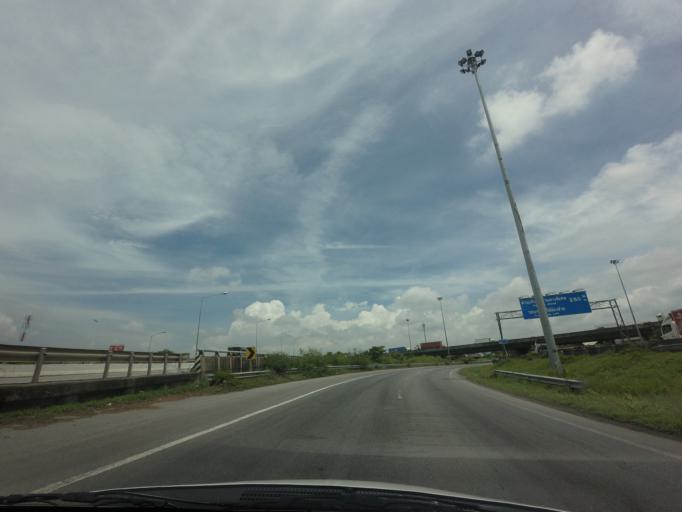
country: TH
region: Bangkok
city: Thung Khru
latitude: 13.6251
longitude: 100.5229
